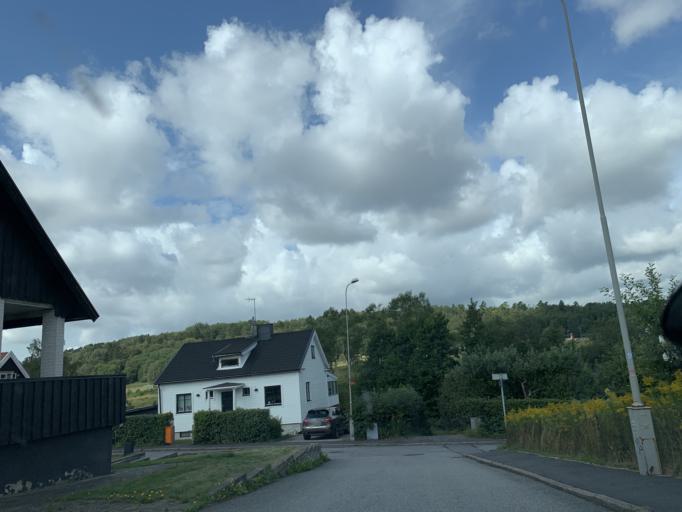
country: SE
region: Vaestra Goetaland
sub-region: Goteborg
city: Eriksbo
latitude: 57.7422
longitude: 12.0491
